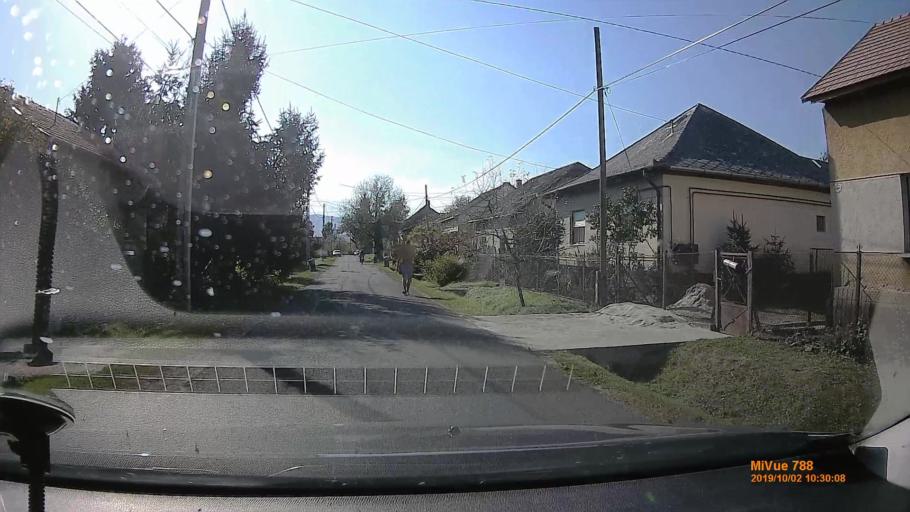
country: HU
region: Nograd
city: Kazar
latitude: 48.0186
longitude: 19.8261
